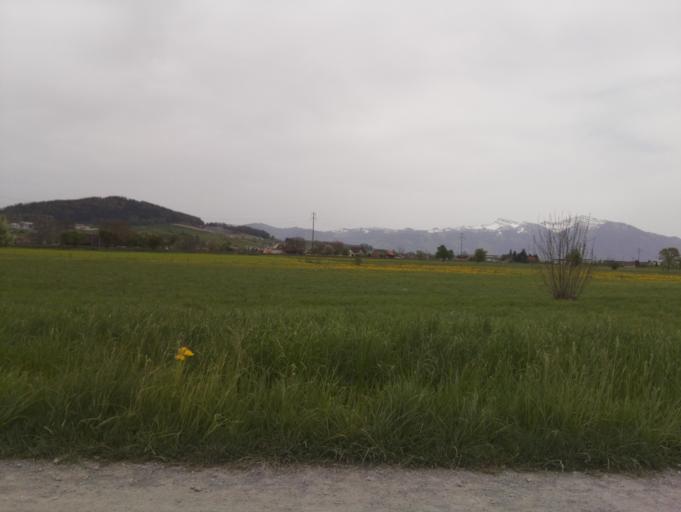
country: CH
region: Schwyz
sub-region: Bezirk March
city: Lachen
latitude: 47.1861
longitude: 8.8802
